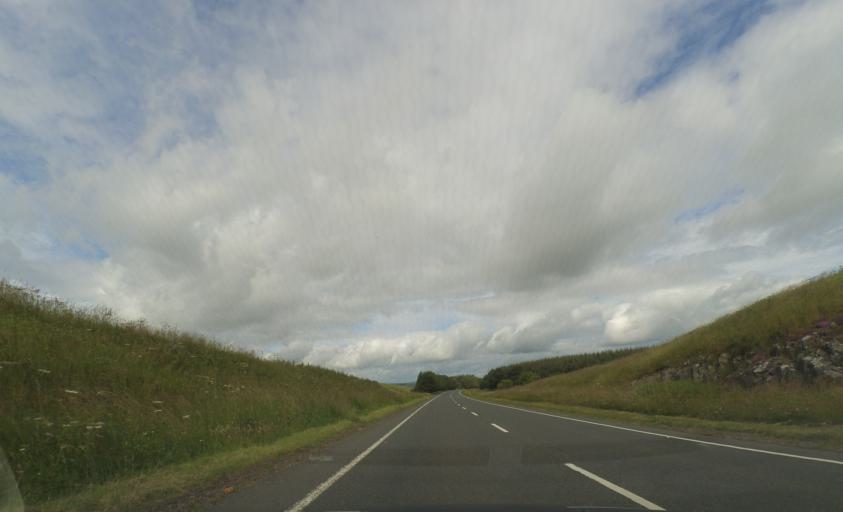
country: GB
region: Scotland
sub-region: The Scottish Borders
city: Hawick
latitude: 55.4749
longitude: -2.8086
